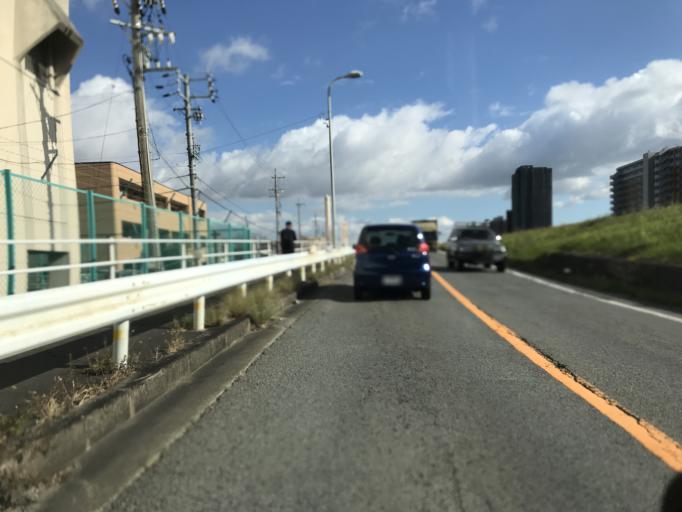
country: JP
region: Aichi
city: Nagoya-shi
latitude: 35.2260
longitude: 136.8760
